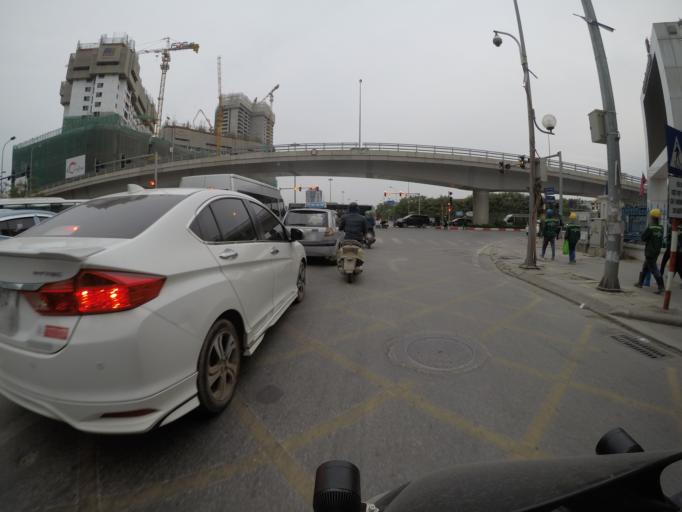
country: VN
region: Ha Noi
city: Thanh Xuan
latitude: 21.0080
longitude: 105.7960
